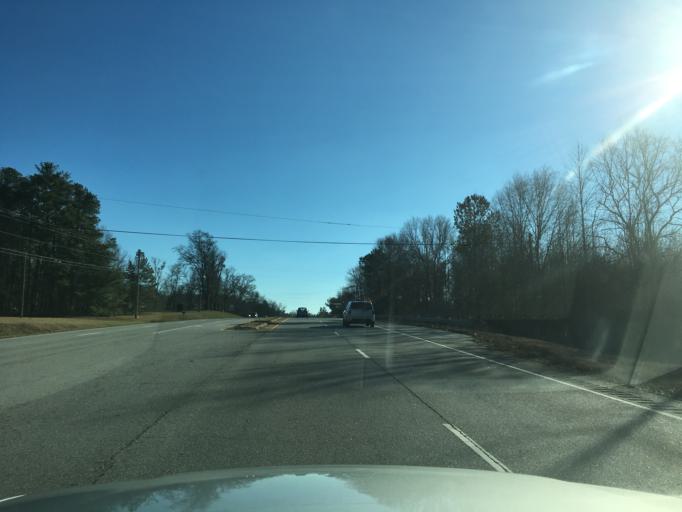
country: US
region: Georgia
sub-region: Carroll County
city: Carrollton
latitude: 33.5305
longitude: -85.0744
